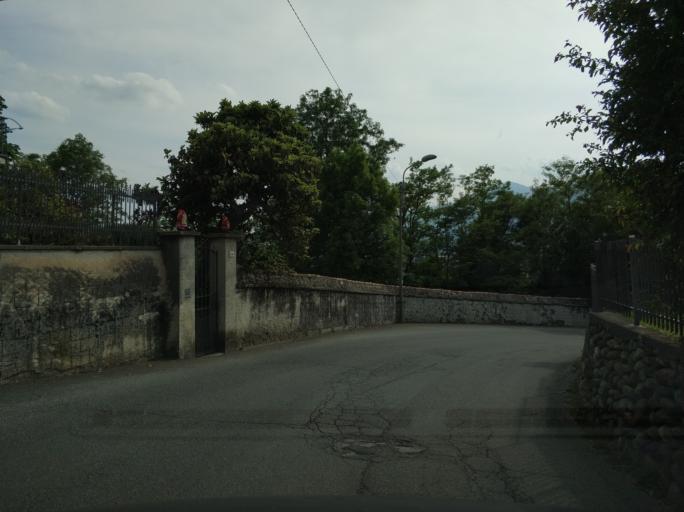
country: IT
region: Piedmont
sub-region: Provincia di Torino
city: Grosso
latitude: 45.2674
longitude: 7.5504
